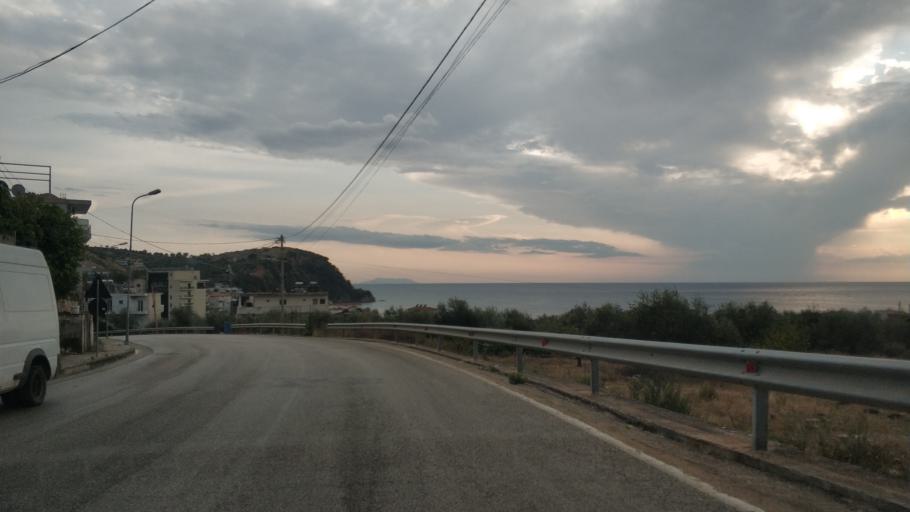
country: AL
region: Vlore
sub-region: Rrethi i Vlores
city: Himare
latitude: 40.0959
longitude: 19.7598
